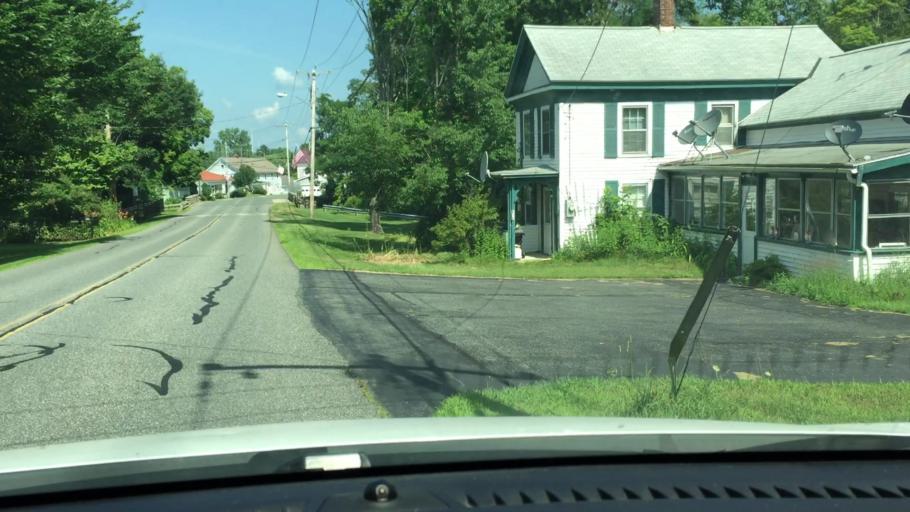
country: US
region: Massachusetts
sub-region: Berkshire County
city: Lee
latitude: 42.2448
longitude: -73.2025
